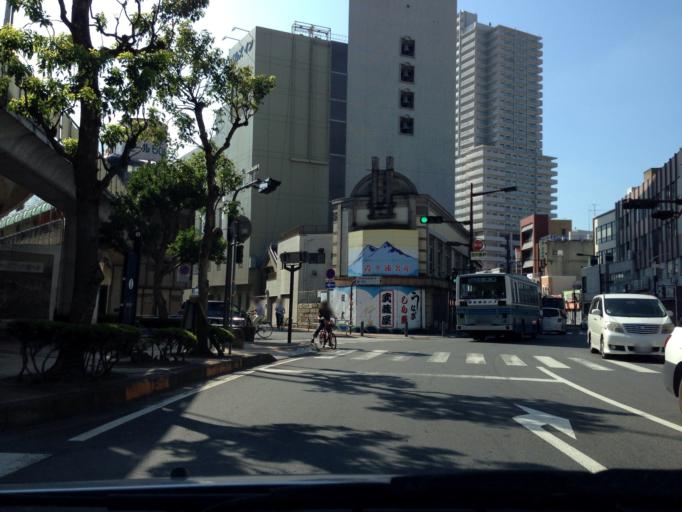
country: JP
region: Ibaraki
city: Naka
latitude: 36.0806
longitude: 140.2026
